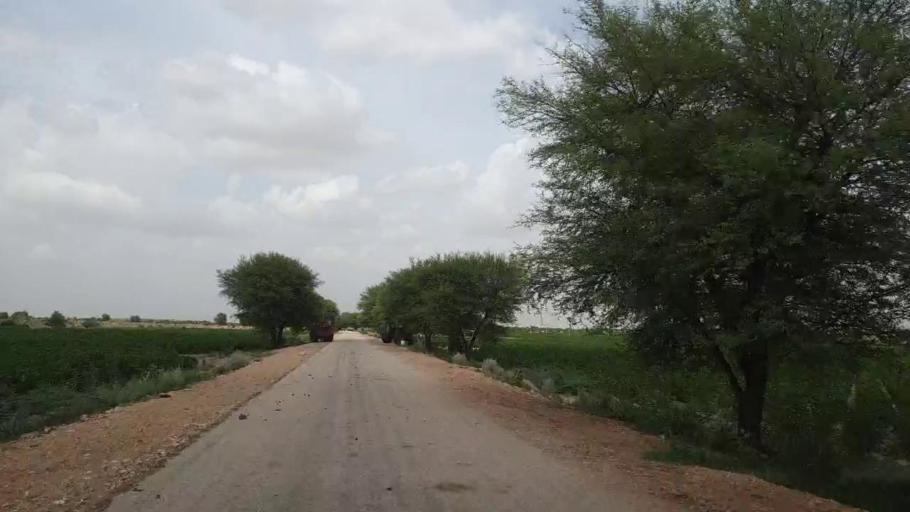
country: PK
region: Sindh
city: Kot Diji
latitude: 27.2259
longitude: 69.0872
